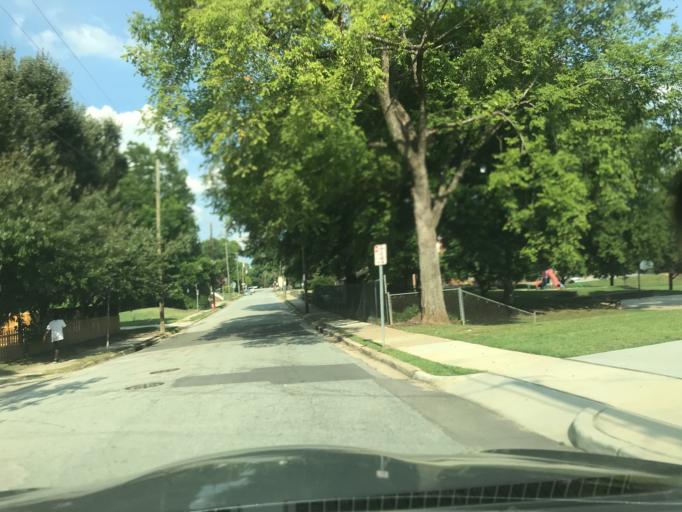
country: US
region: North Carolina
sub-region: Wake County
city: Raleigh
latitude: 35.7752
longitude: -78.6252
